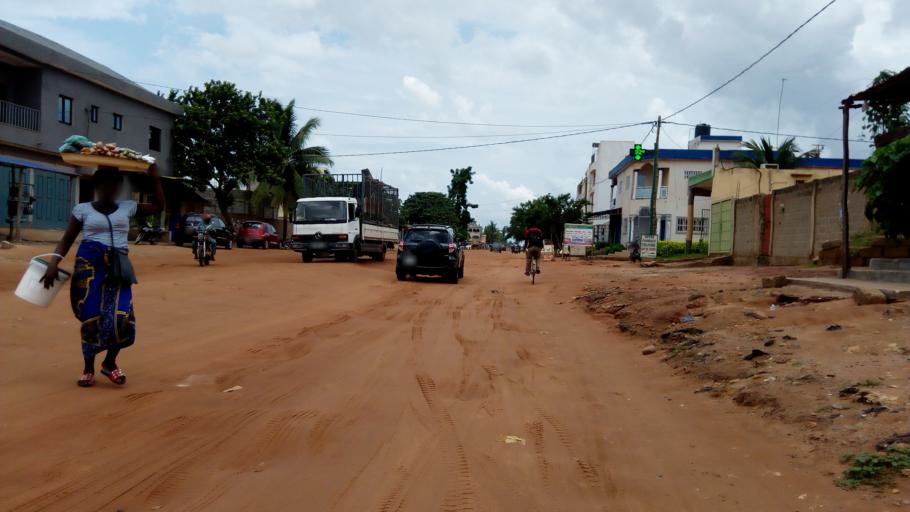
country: TG
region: Maritime
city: Lome
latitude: 6.2217
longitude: 1.1654
